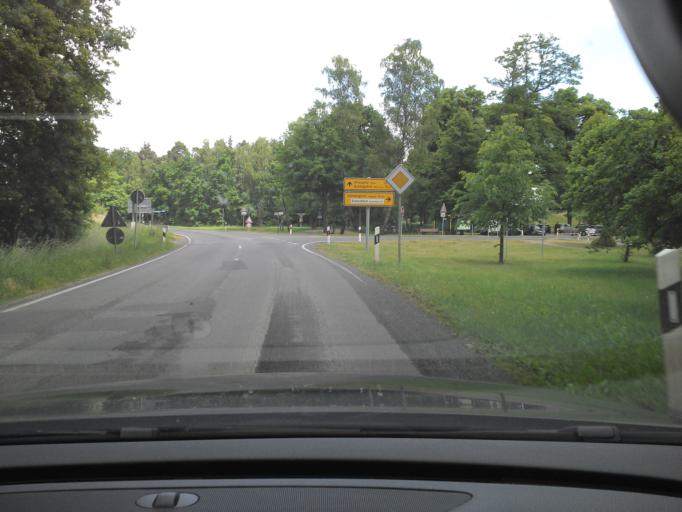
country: DE
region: Brandenburg
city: Burg
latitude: 51.8449
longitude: 14.1550
